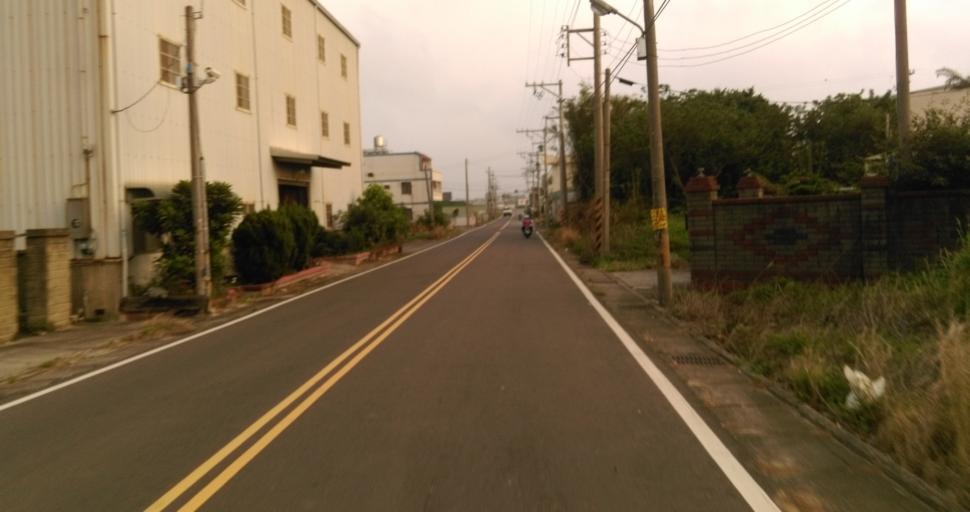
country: TW
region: Taiwan
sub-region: Hsinchu
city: Zhubei
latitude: 24.8752
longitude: 120.9554
